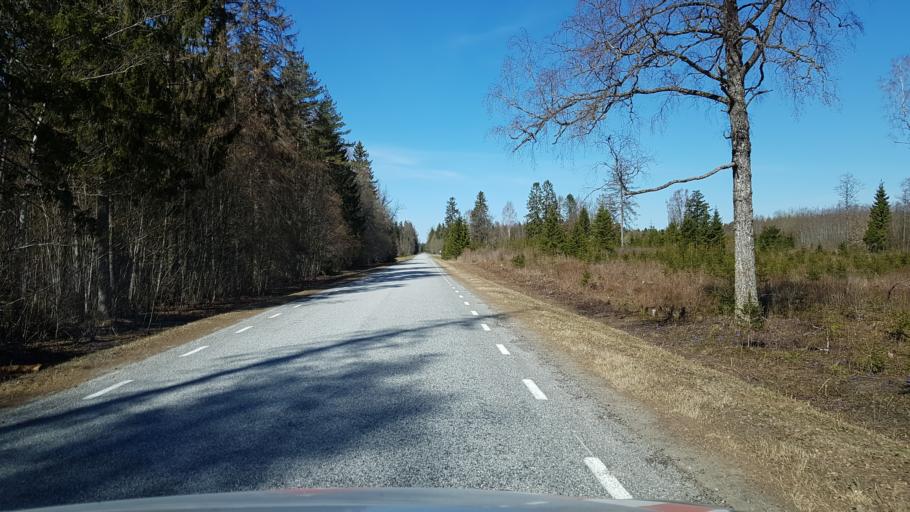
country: EE
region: Laeaene-Virumaa
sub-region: Vinni vald
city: Vinni
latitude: 59.1630
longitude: 26.5116
